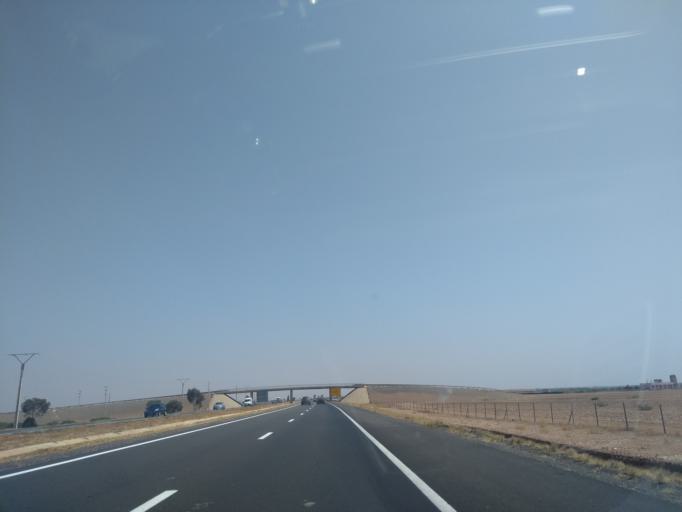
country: MA
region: Marrakech-Tensift-Al Haouz
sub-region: Kelaa-Des-Sraghna
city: Sidi Bou Othmane
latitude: 31.9337
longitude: -8.0179
